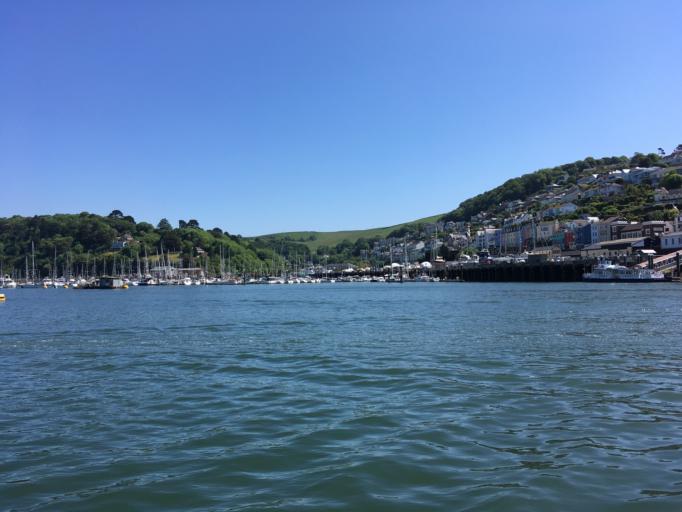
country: GB
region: England
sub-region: Devon
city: Dartmouth
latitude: 50.3488
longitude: -3.5760
